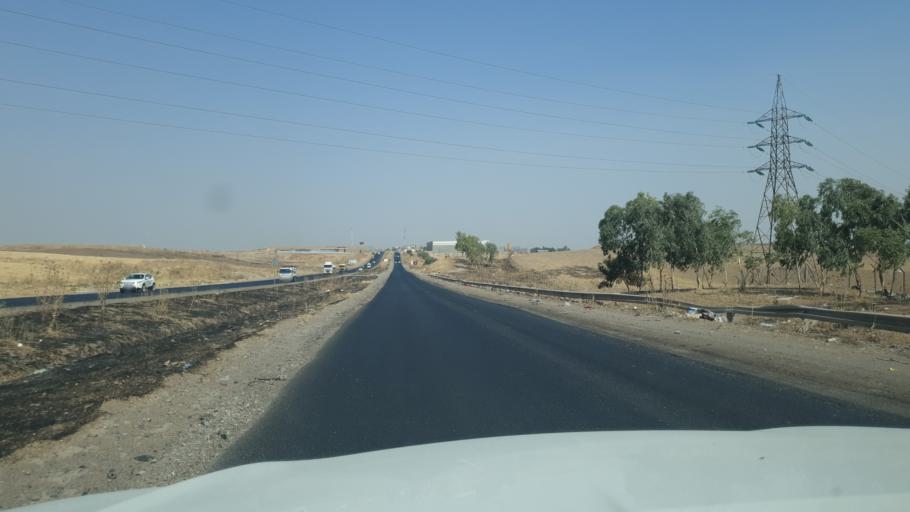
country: IQ
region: Arbil
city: Erbil
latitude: 36.1981
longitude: 43.8860
